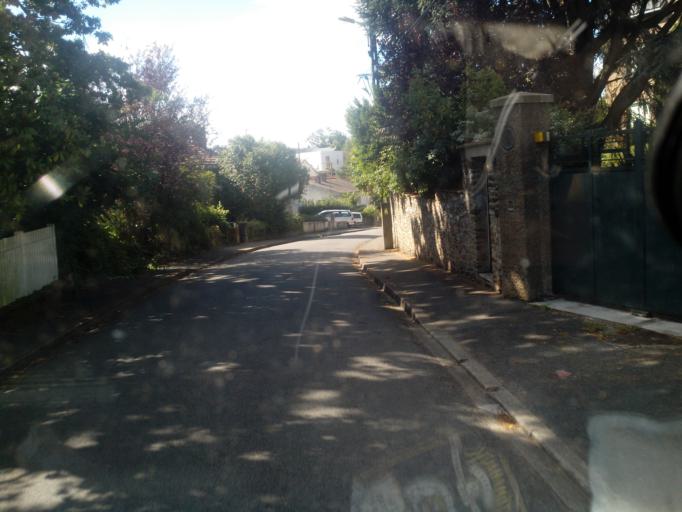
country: FR
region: Pays de la Loire
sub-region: Departement de la Loire-Atlantique
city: Nantes
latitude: 47.2515
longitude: -1.5792
